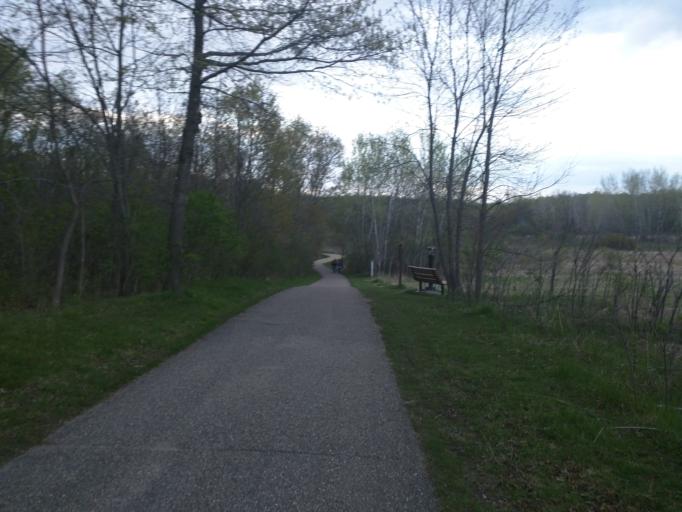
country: US
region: Minnesota
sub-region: Hennepin County
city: Minnetonka
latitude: 44.9011
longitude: -93.5030
